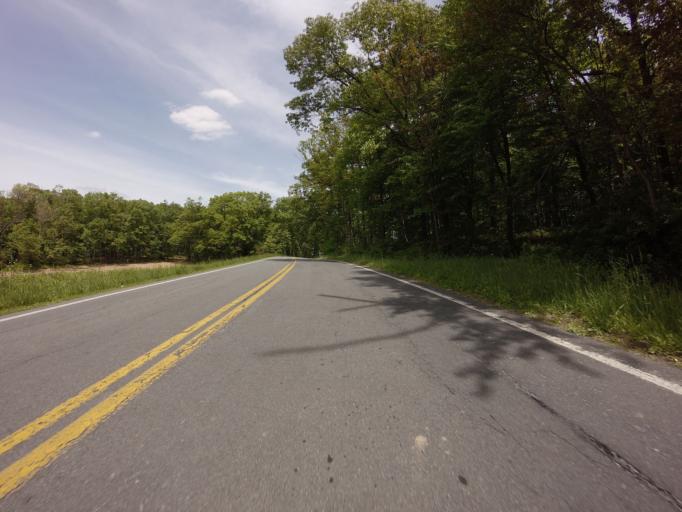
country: US
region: Maryland
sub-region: Frederick County
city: Woodsboro
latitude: 39.5197
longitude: -77.2632
